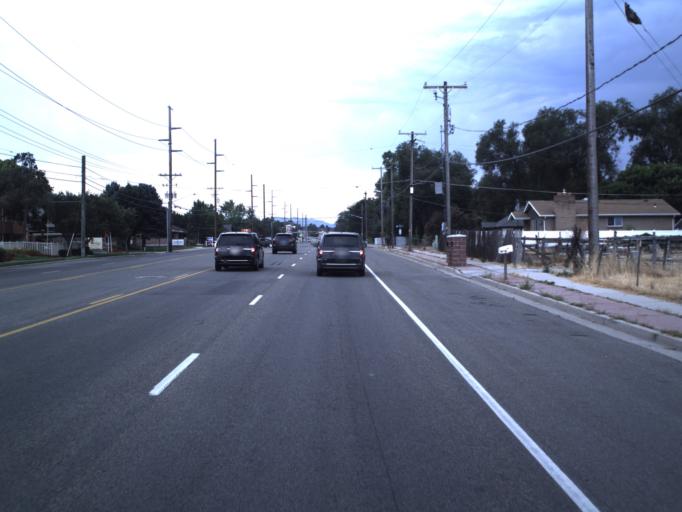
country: US
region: Utah
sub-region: Salt Lake County
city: Midvale
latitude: 40.6278
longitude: -111.8661
